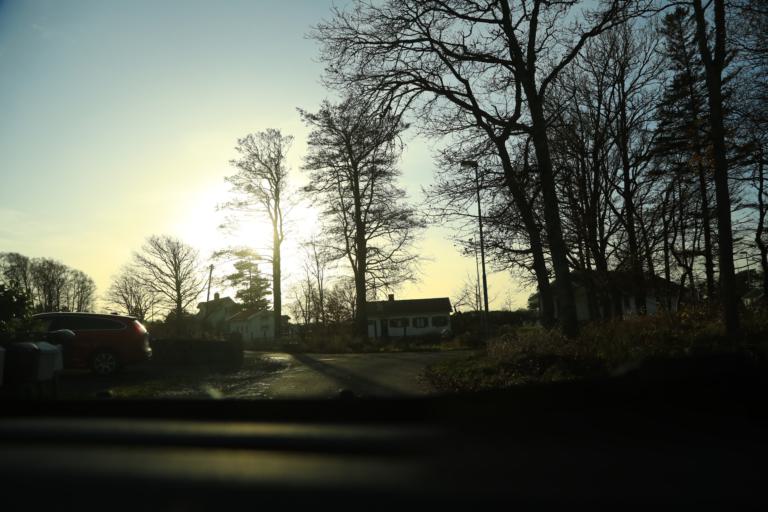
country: SE
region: Halland
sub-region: Varbergs Kommun
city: Varberg
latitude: 57.1895
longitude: 12.2131
